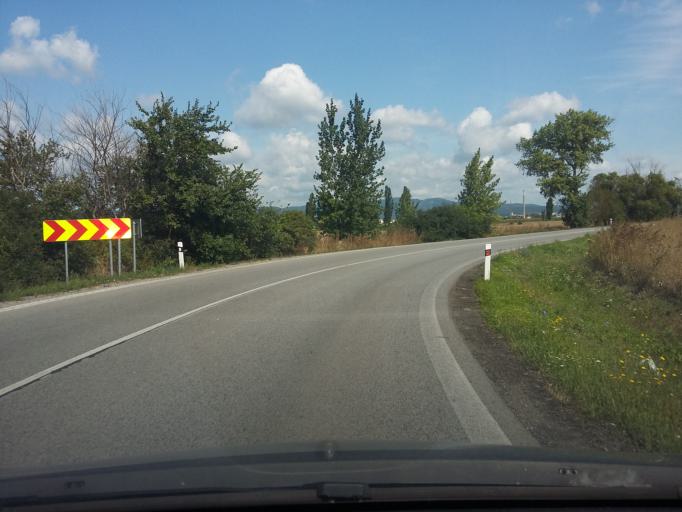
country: SK
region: Bratislavsky
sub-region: Okres Pezinok
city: Pezinok
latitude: 48.2537
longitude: 17.2609
